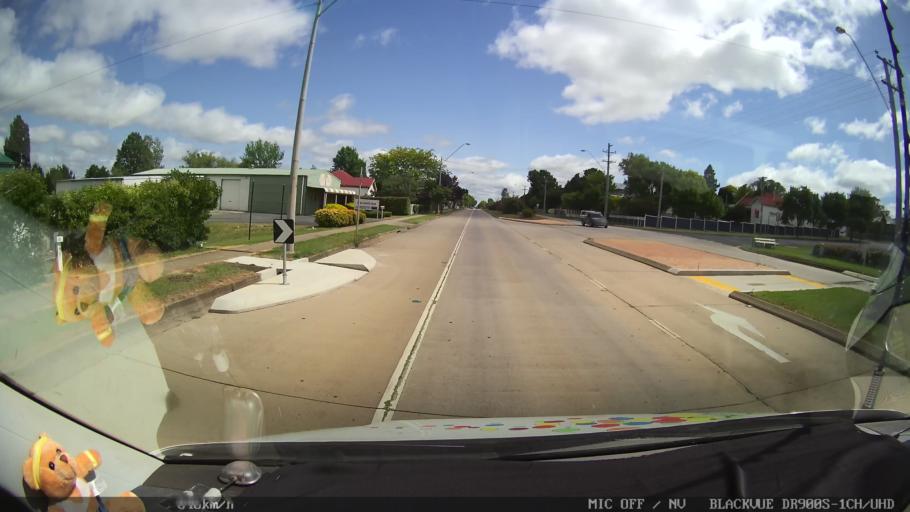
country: AU
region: New South Wales
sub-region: Glen Innes Severn
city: Glen Innes
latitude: -29.7463
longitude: 151.7365
